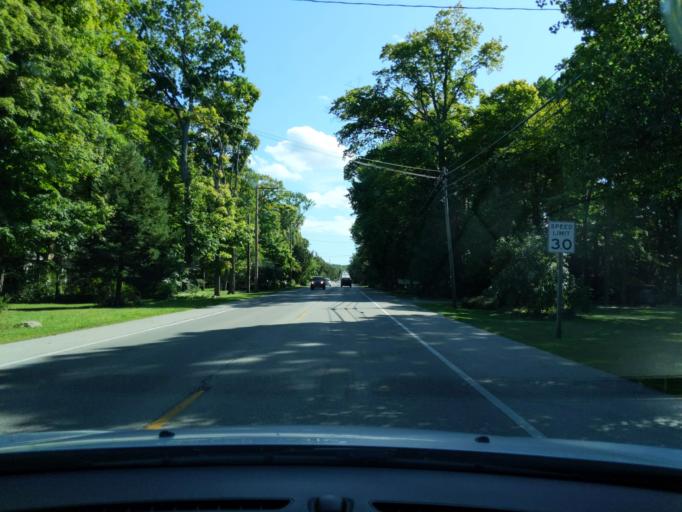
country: US
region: Wisconsin
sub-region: Door County
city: Sturgeon Bay
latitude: 45.1985
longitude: -87.1189
